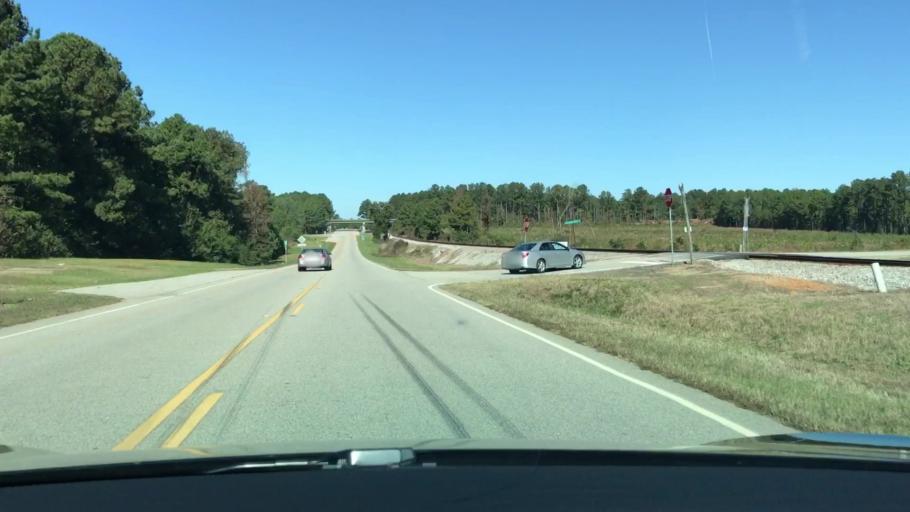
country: US
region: Georgia
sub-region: Taliaferro County
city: Crawfordville
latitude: 33.4940
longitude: -82.8005
